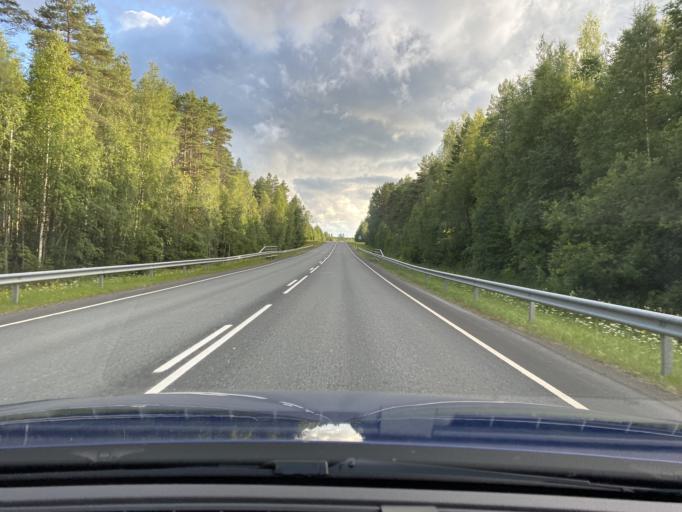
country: FI
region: Haeme
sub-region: Haemeenlinna
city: Renko
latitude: 60.8548
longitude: 24.1637
